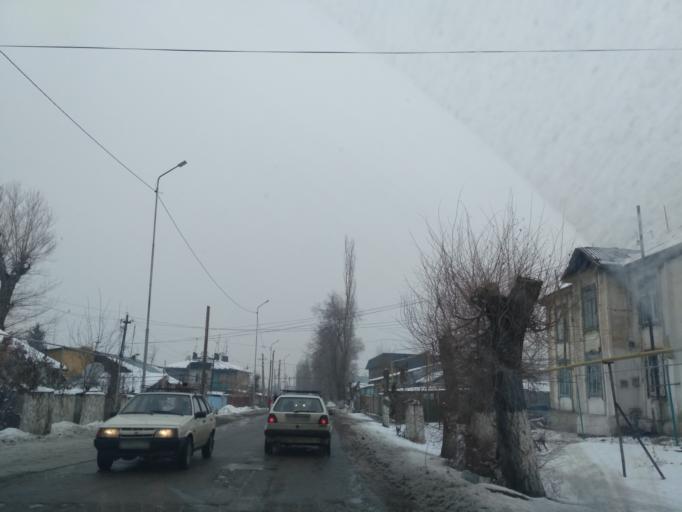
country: KZ
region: Almaty Oblysy
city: Burunday
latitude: 43.1571
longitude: 76.4147
